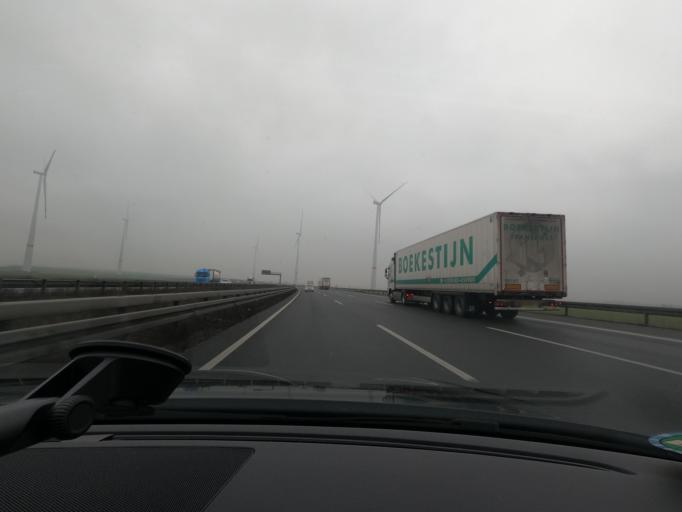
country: DE
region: North Rhine-Westphalia
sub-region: Regierungsbezirk Dusseldorf
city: Juchen
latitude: 51.0480
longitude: 6.5003
